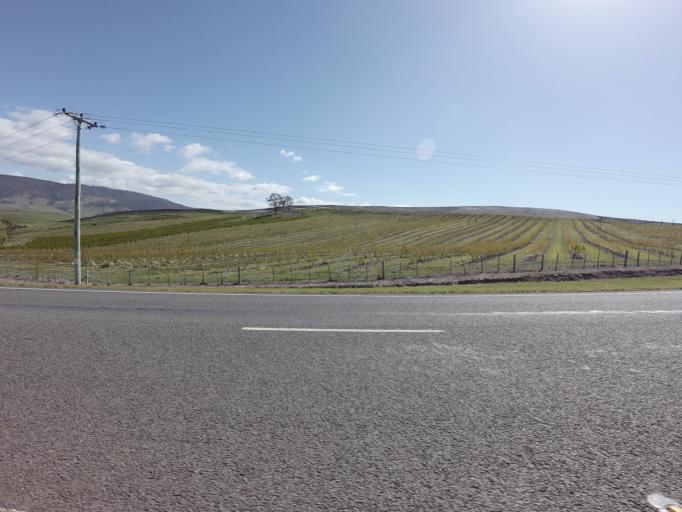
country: AU
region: Tasmania
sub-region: Derwent Valley
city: New Norfolk
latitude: -42.7124
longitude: 146.9470
